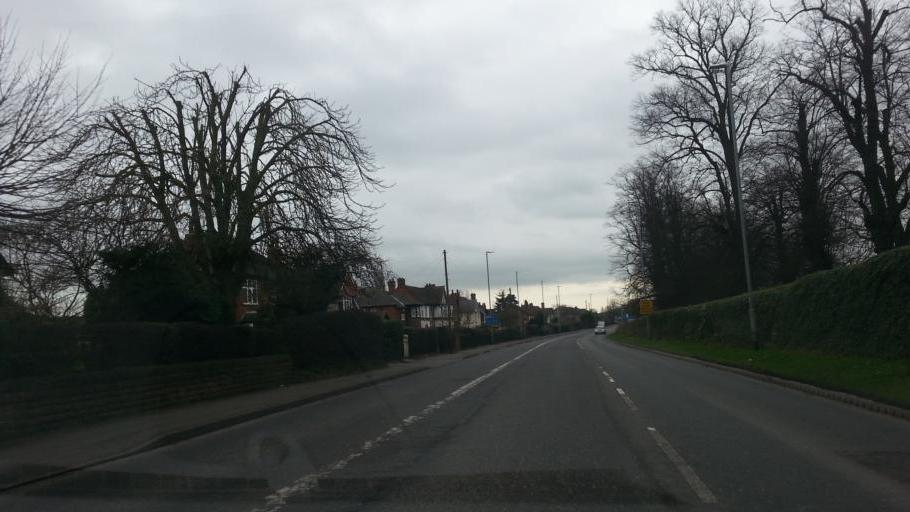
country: GB
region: England
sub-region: Nottinghamshire
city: Kimberley
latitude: 52.9937
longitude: -1.2278
